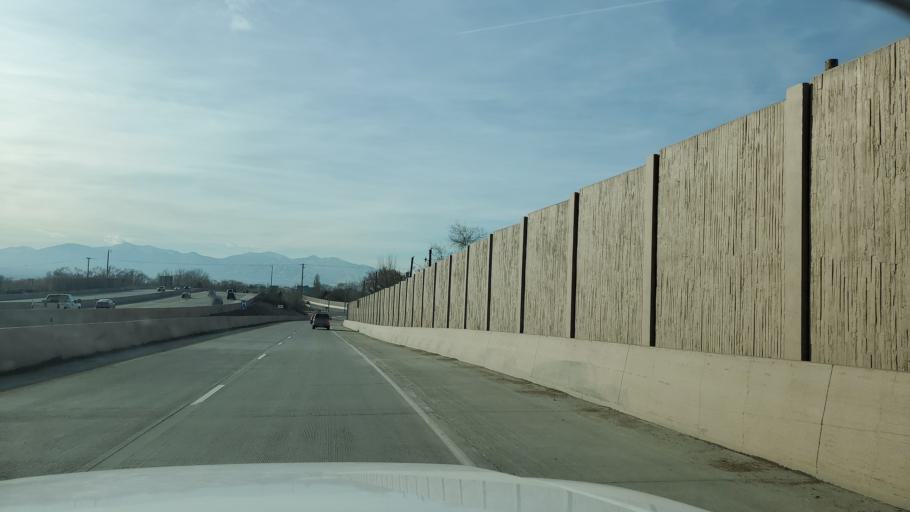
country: US
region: Utah
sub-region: Salt Lake County
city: South Salt Lake
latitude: 40.7200
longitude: -111.8687
